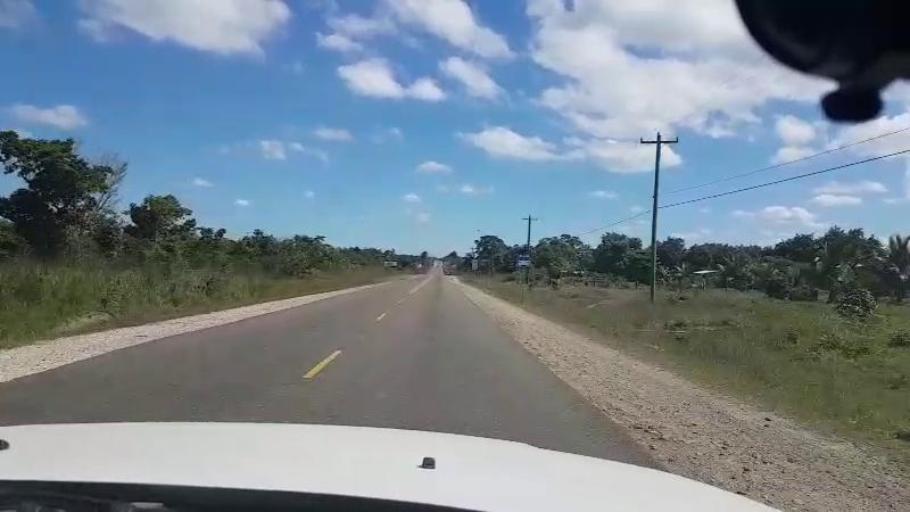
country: BZ
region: Cayo
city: Belmopan
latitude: 17.2771
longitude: -88.6722
